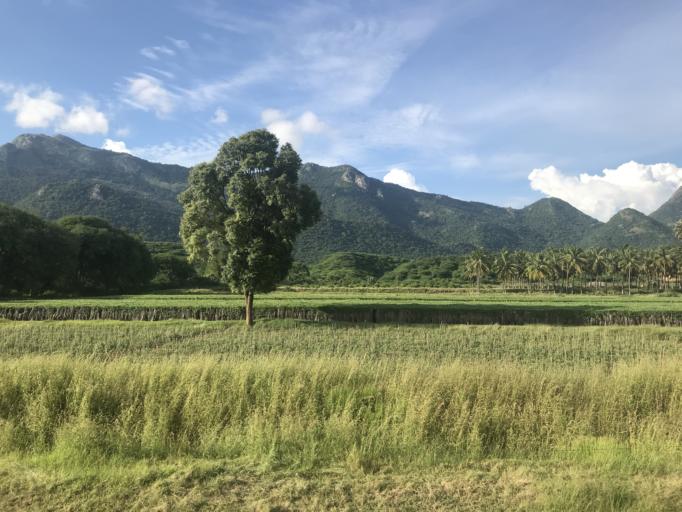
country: IN
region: Tamil Nadu
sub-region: Coimbatore
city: Madukkarai
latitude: 10.8769
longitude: 76.8598
